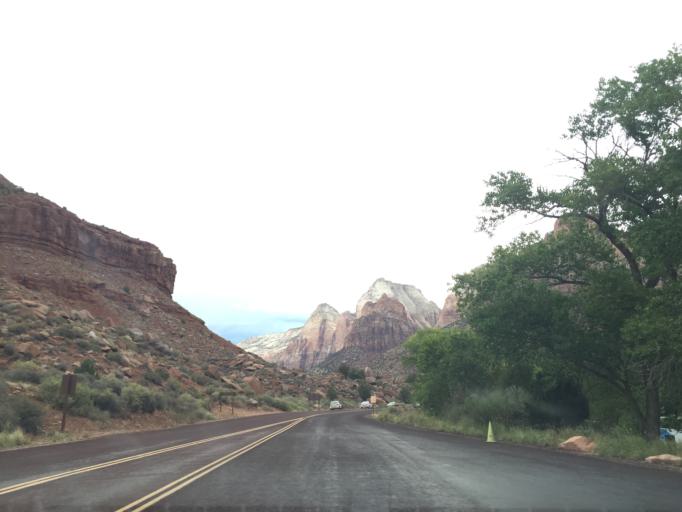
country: US
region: Utah
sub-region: Washington County
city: Hildale
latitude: 37.2029
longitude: -112.9875
